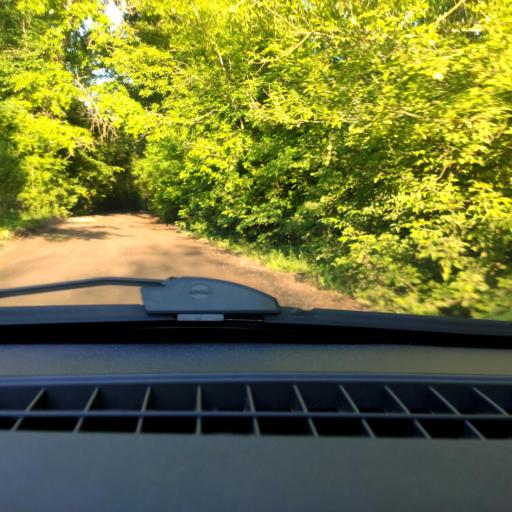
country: RU
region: Bashkortostan
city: Avdon
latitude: 54.6089
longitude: 55.6672
